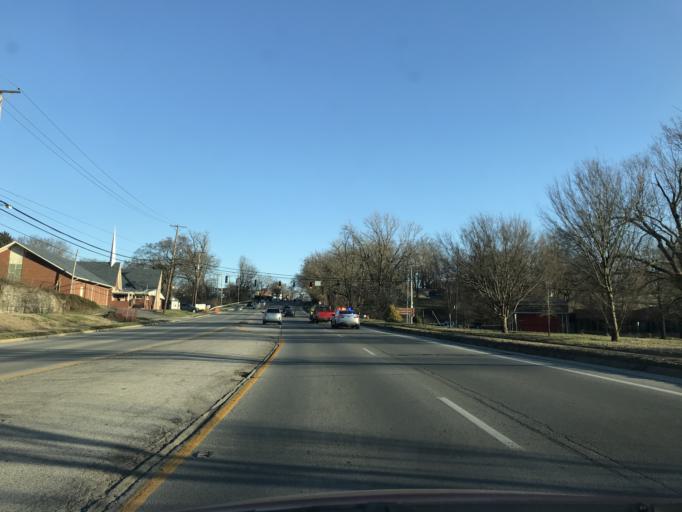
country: US
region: Kentucky
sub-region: Jefferson County
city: Audubon Park
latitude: 38.2083
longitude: -85.7159
